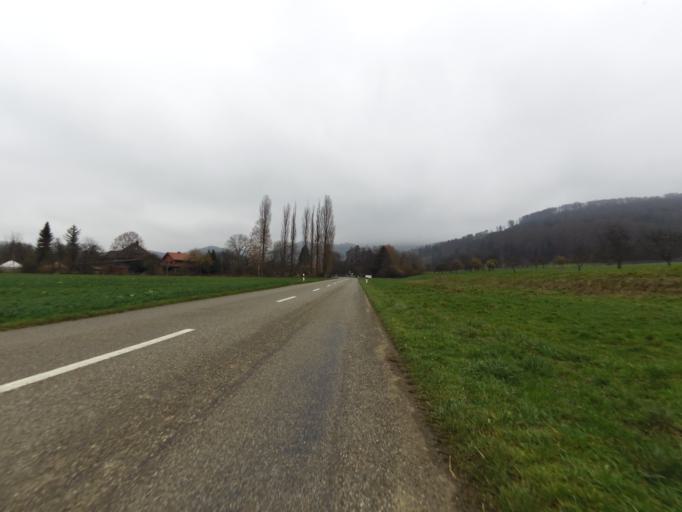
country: CH
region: Jura
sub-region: Porrentruy District
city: Alle
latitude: 47.4123
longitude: 7.1882
